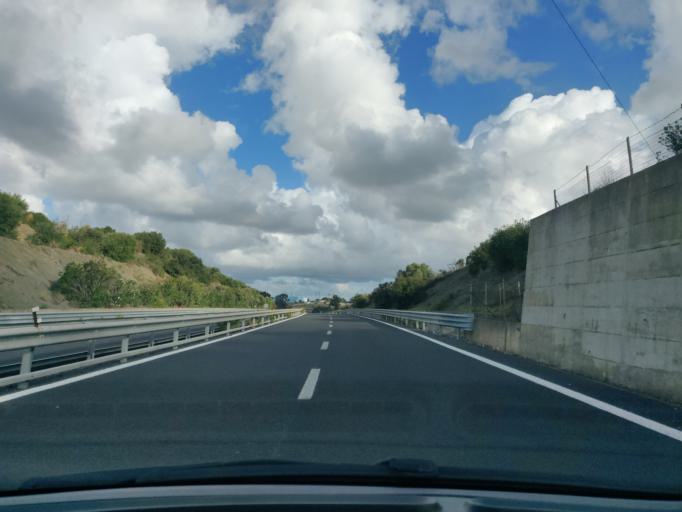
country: IT
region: Latium
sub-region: Citta metropolitana di Roma Capitale
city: Civitavecchia
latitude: 42.1141
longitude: 11.7924
